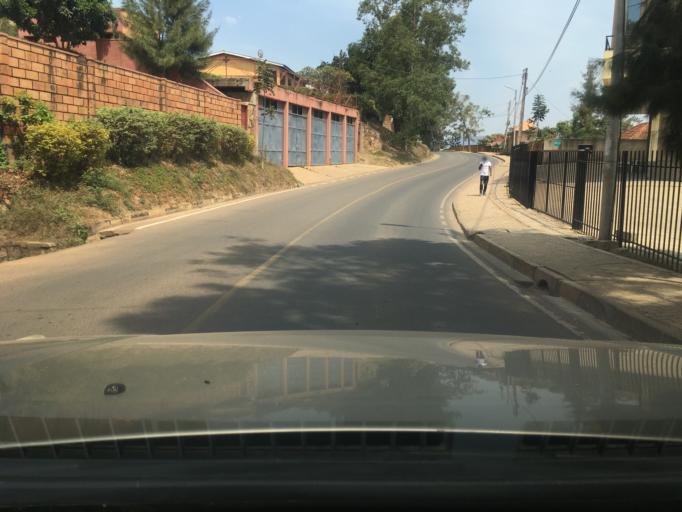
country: RW
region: Kigali
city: Kigali
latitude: -1.9619
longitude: 30.1038
